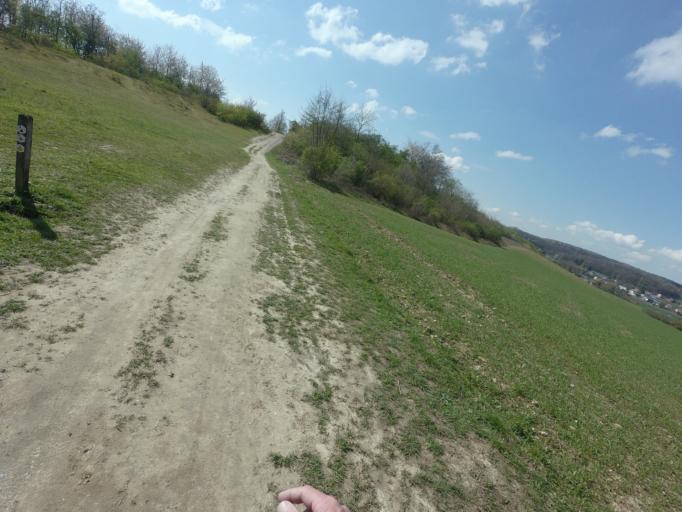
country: NL
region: Limburg
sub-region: Gemeente Maastricht
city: Maastricht
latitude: 50.8175
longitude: 5.6820
